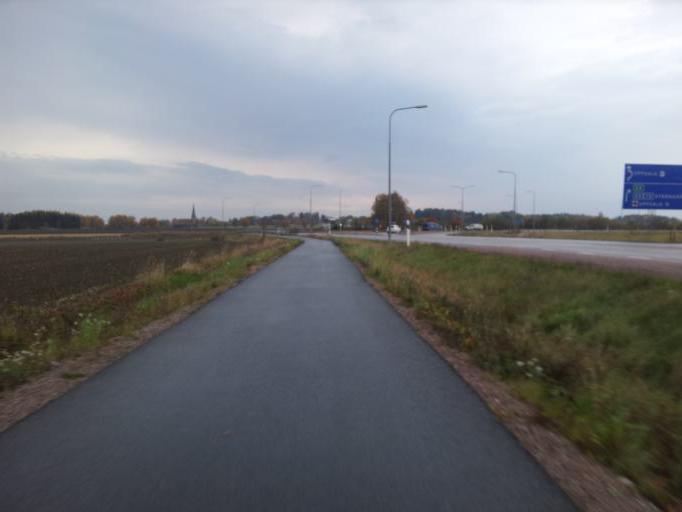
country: SE
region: Uppsala
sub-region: Uppsala Kommun
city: Gamla Uppsala
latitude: 59.8882
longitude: 17.6958
